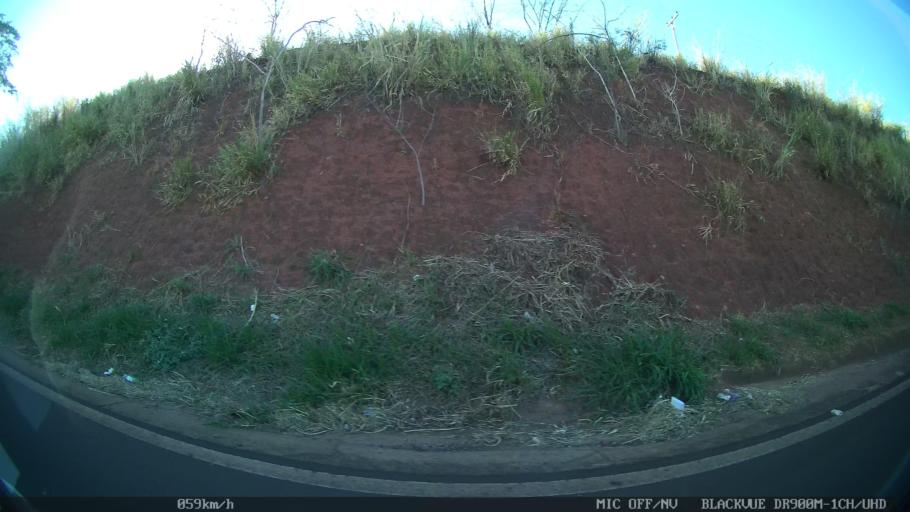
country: BR
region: Sao Paulo
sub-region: Guapiacu
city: Guapiacu
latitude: -20.7823
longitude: -49.2638
